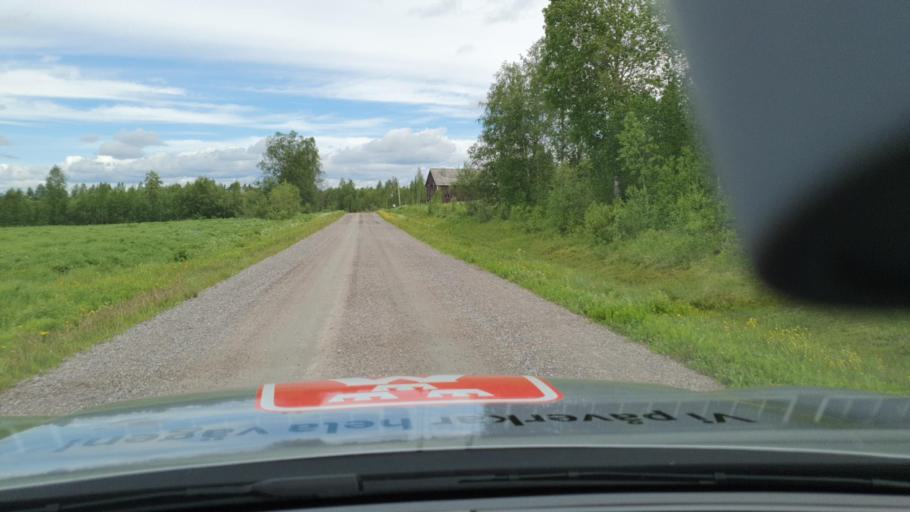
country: FI
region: Lapland
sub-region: Torniolaakso
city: Ylitornio
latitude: 65.9733
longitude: 23.7931
